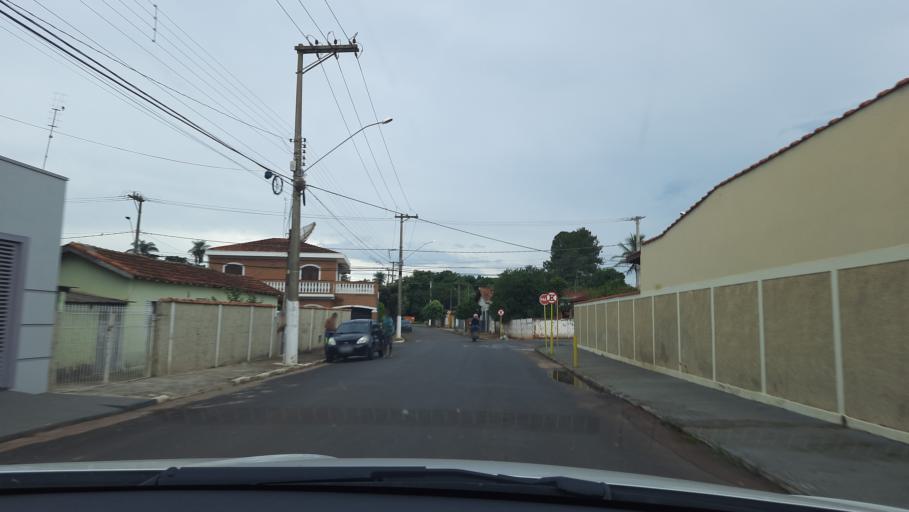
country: BR
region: Sao Paulo
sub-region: Casa Branca
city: Casa Branca
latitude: -21.7684
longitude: -47.0899
